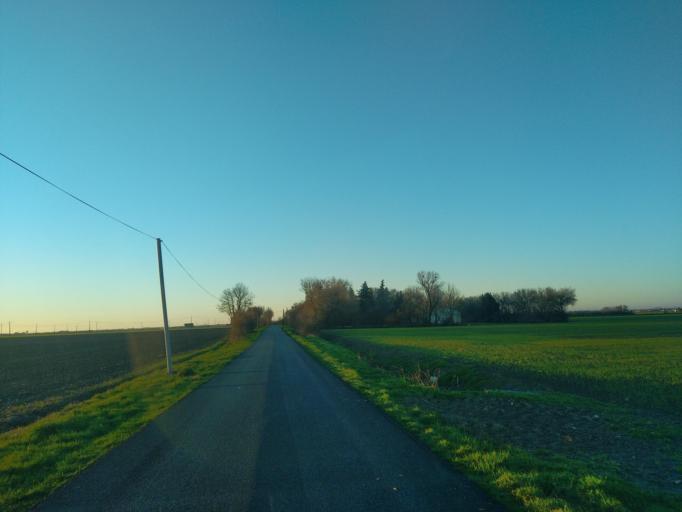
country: FR
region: Pays de la Loire
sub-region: Departement de la Vendee
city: Angles
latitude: 46.3754
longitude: -1.3030
